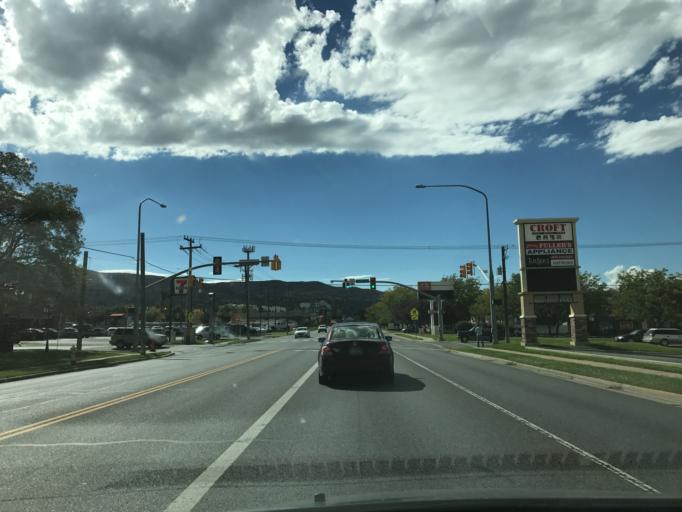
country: US
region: Utah
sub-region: Davis County
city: Woods Cross
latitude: 40.8752
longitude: -111.8923
